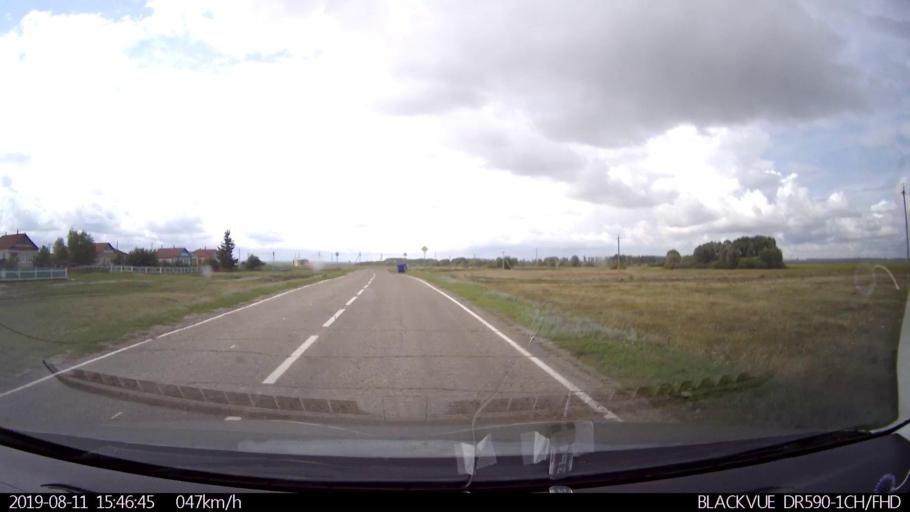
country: RU
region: Ulyanovsk
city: Ignatovka
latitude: 53.8840
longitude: 47.6545
